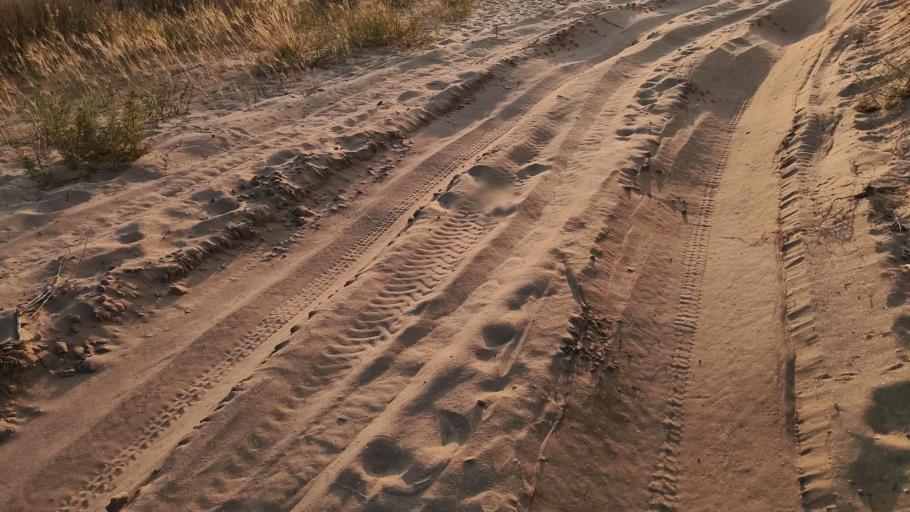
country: RU
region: Krasnodarskiy
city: Blagovetschenskaya
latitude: 45.0668
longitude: 37.0385
